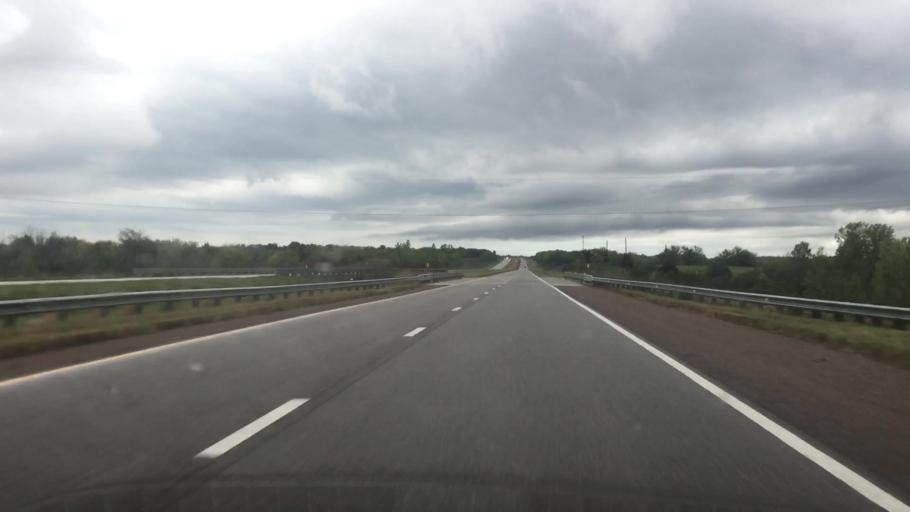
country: US
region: Kansas
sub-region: Miami County
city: Paola
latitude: 38.6075
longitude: -94.8356
